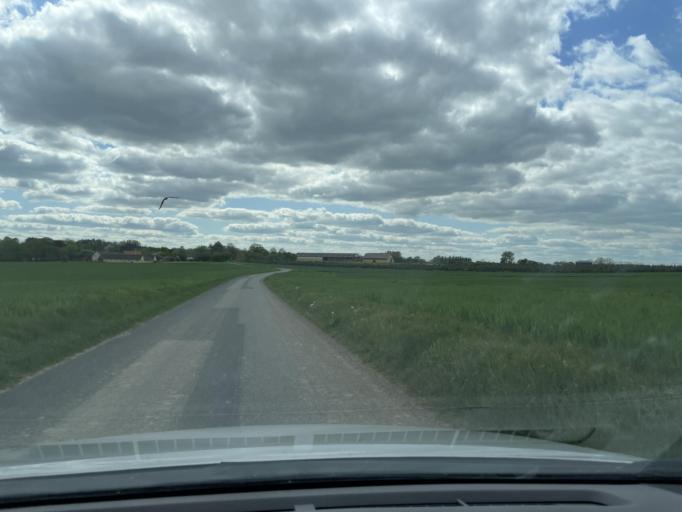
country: DK
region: Central Jutland
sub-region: Skanderborg Kommune
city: Skanderborg
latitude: 55.9231
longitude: 9.9734
